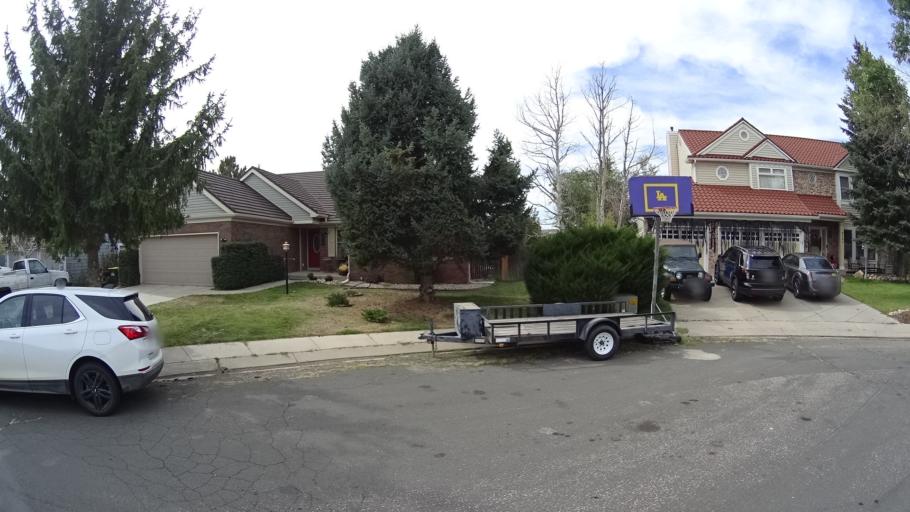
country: US
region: Colorado
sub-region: El Paso County
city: Cimarron Hills
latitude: 38.9007
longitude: -104.7041
